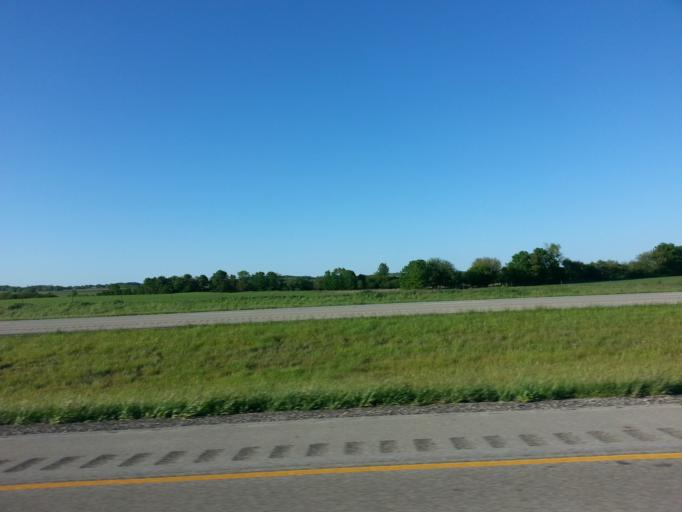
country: US
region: Illinois
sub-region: McLean County
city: Downs
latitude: 40.3803
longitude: -88.8544
